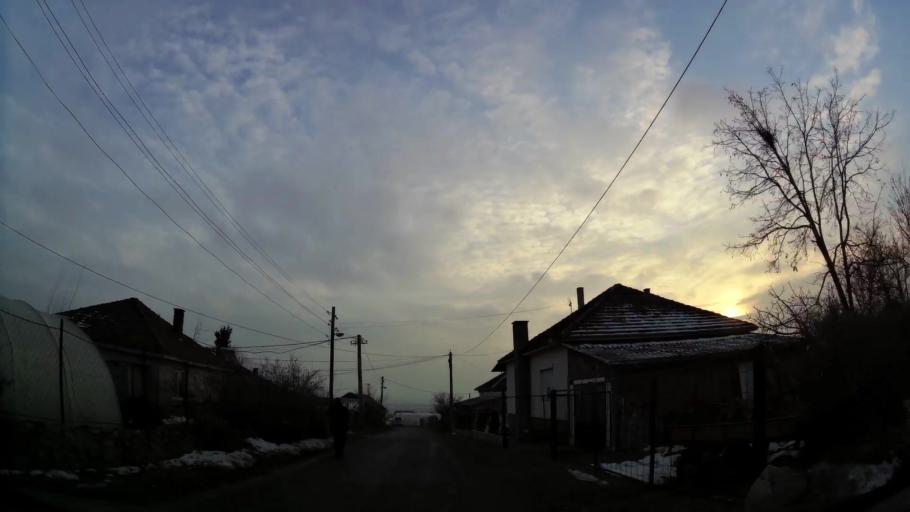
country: MK
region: Aracinovo
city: Arachinovo
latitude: 42.0327
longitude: 21.5464
